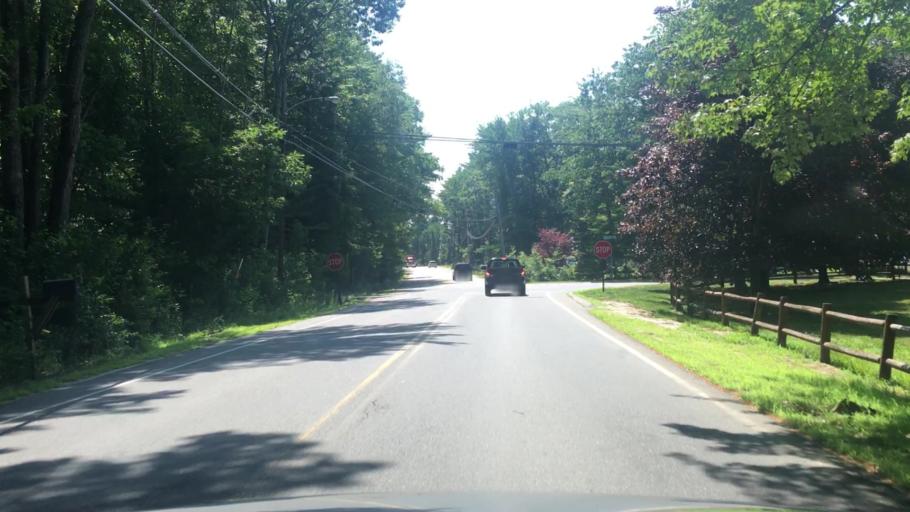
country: US
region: Maine
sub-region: Cumberland County
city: Cumberland Center
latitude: 43.8226
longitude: -70.2995
